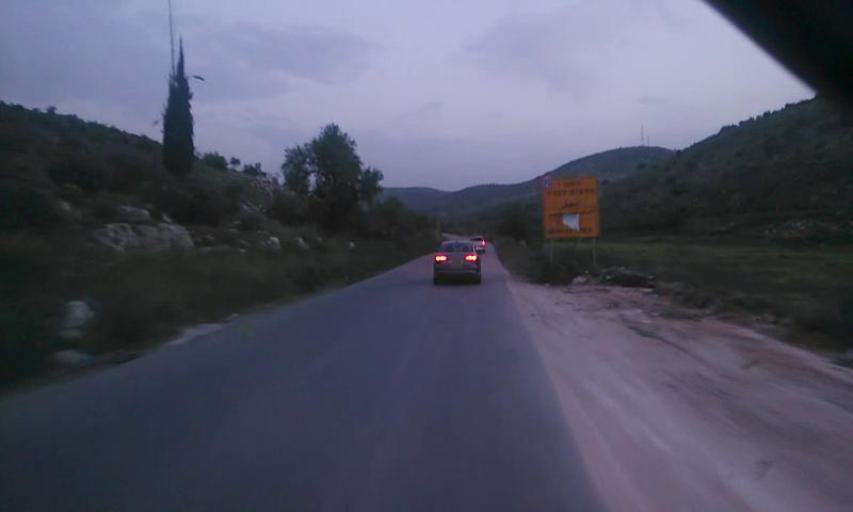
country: PS
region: West Bank
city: Ramin
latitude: 32.2945
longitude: 35.1332
